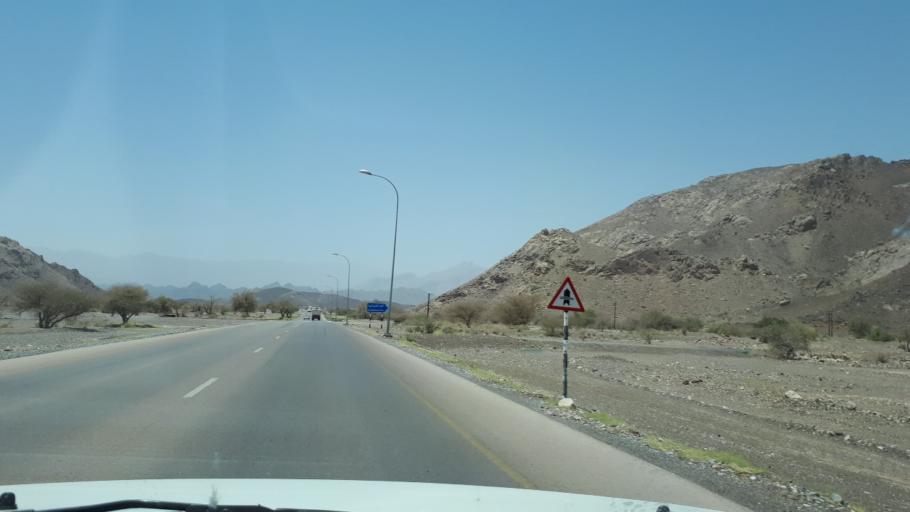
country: OM
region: Muhafazat ad Dakhiliyah
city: Bahla'
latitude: 23.0535
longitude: 57.2999
